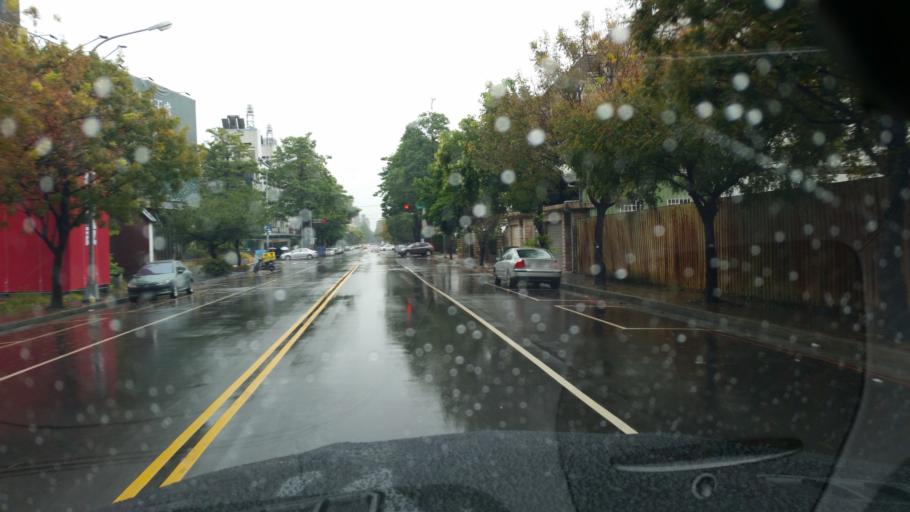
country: TW
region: Taiwan
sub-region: Taichung City
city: Taichung
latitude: 24.1555
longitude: 120.6439
